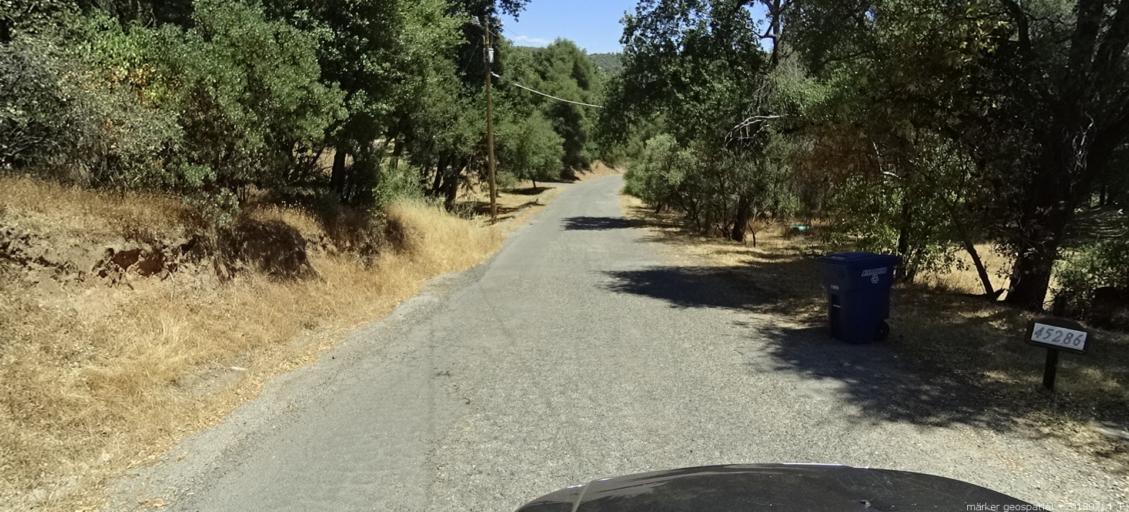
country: US
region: California
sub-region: Madera County
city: Ahwahnee
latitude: 37.4073
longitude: -119.7189
